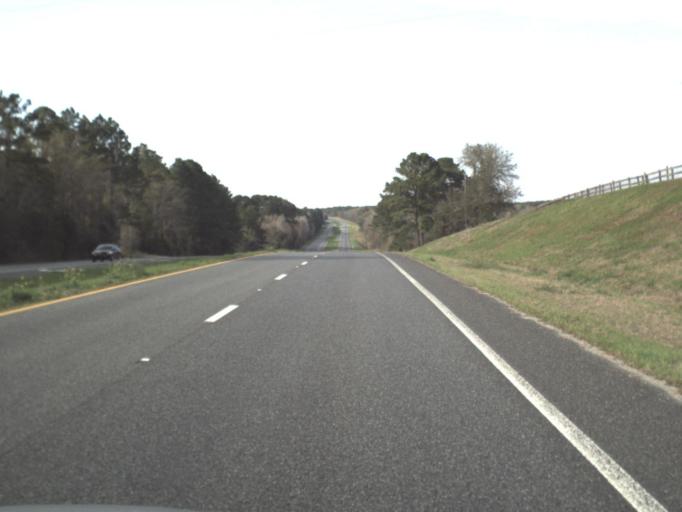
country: US
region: Florida
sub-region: Jefferson County
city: Monticello
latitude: 30.6193
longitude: -83.8722
